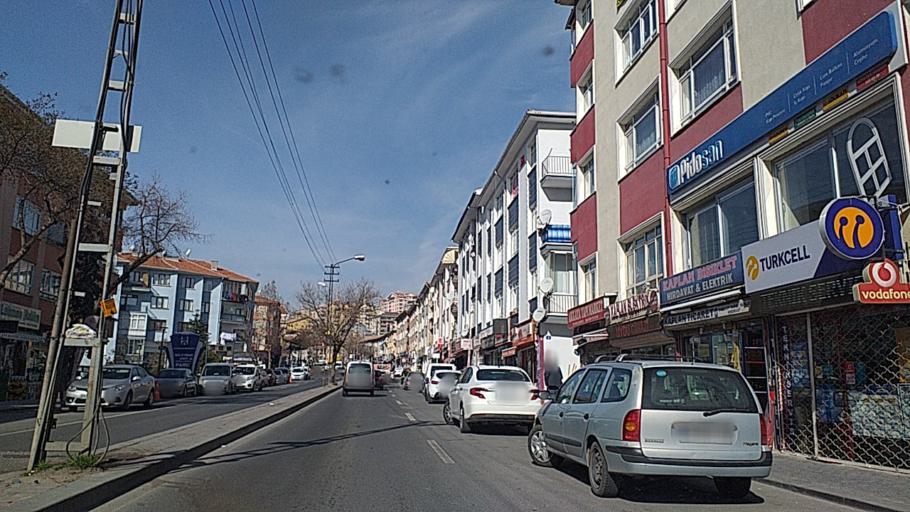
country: TR
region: Ankara
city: Ankara
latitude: 39.9838
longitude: 32.8326
